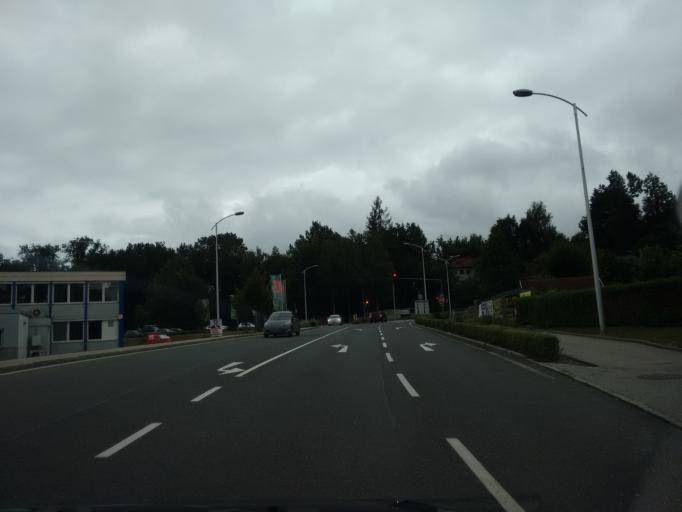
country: AT
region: Upper Austria
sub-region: Politischer Bezirk Grieskirchen
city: Grieskirchen
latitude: 48.2323
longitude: 13.8286
